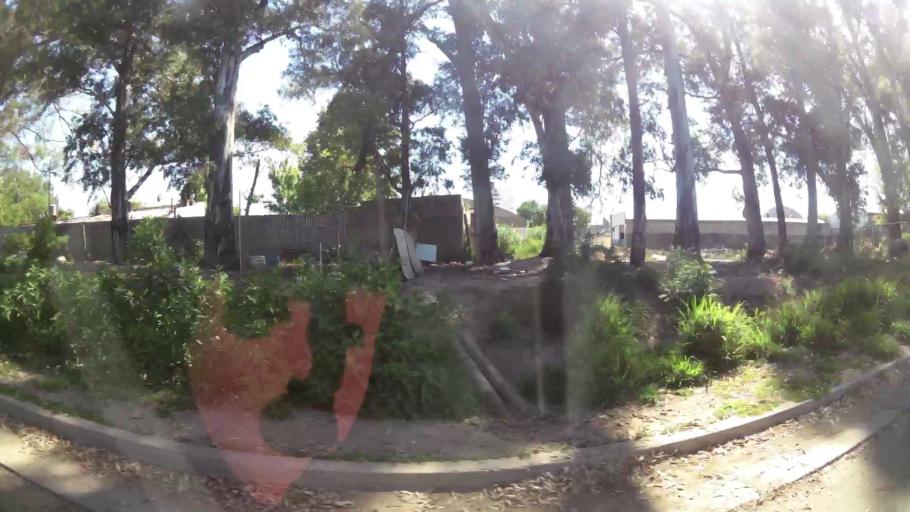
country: AR
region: Cordoba
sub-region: Departamento de Capital
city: Cordoba
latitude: -31.4361
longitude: -64.1336
